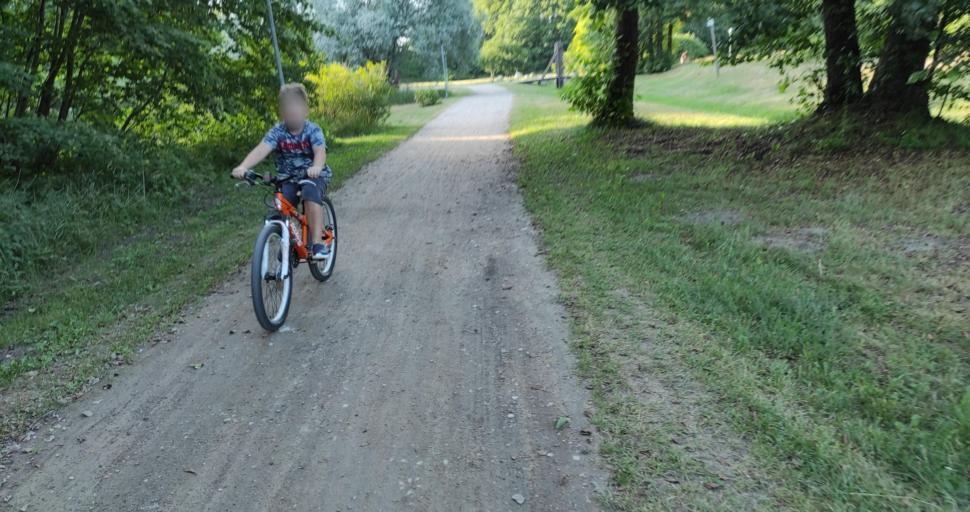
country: LV
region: Ventspils
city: Ventspils
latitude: 57.3858
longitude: 21.5299
